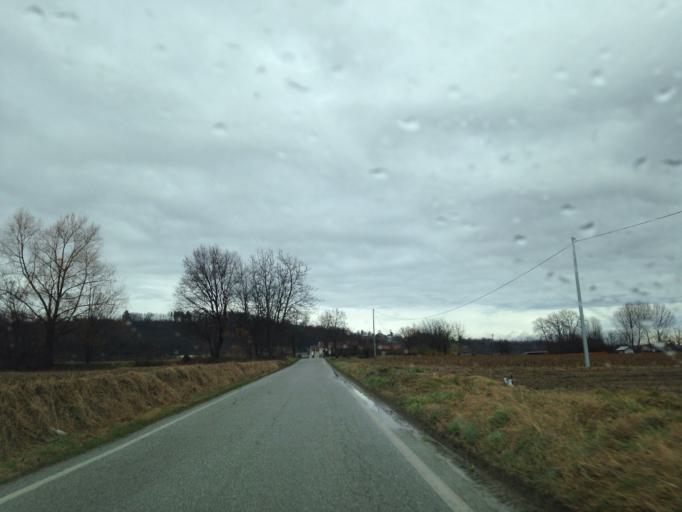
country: IT
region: Piedmont
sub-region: Provincia di Vercelli
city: Moncrivello
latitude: 45.3150
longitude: 7.9949
